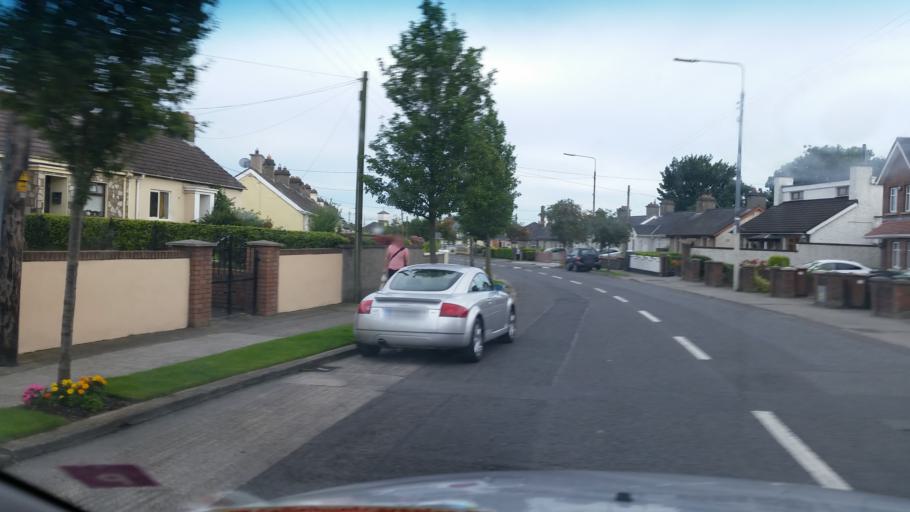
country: IE
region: Leinster
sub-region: Dublin City
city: Finglas
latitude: 53.3927
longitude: -6.3004
